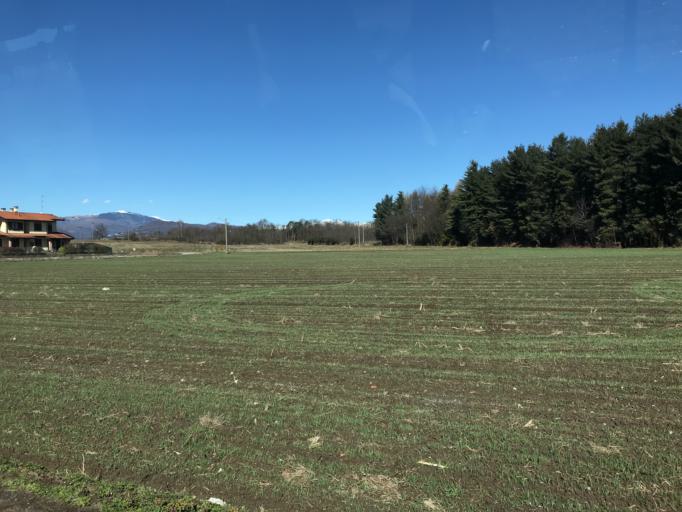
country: IT
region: Lombardy
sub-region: Provincia di Varese
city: Cadrezzate
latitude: 45.7992
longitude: 8.6260
